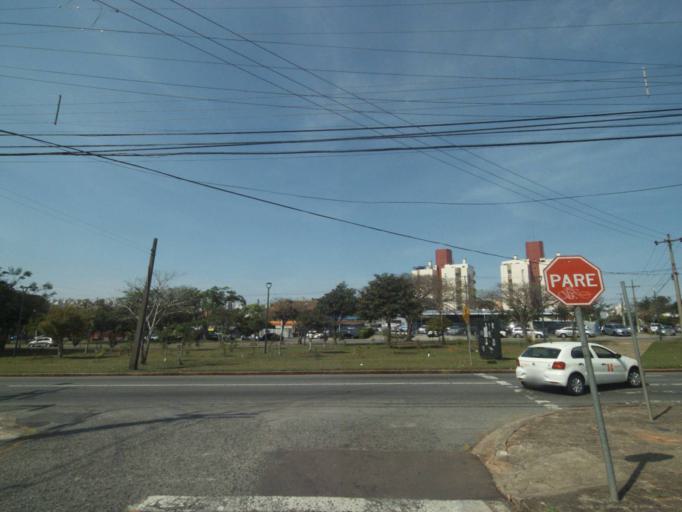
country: BR
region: Parana
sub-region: Curitiba
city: Curitiba
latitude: -25.4610
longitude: -49.3021
